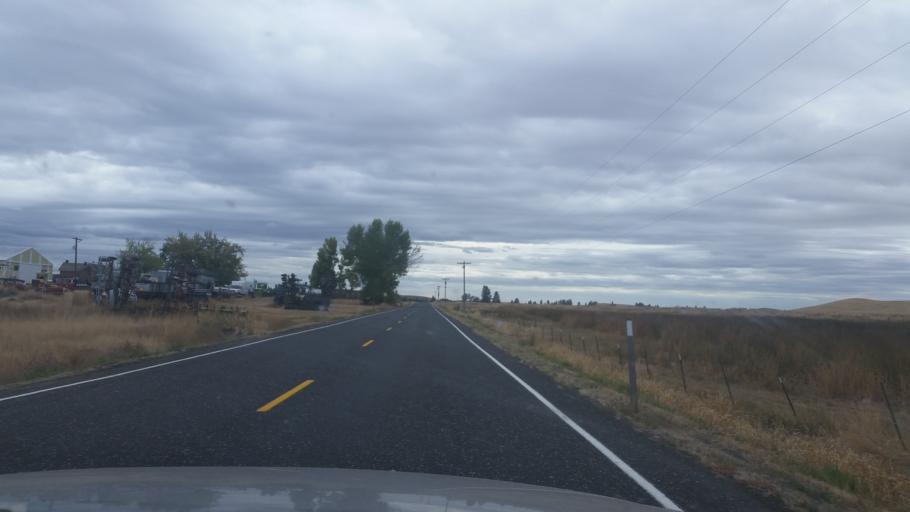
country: US
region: Washington
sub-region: Spokane County
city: Medical Lake
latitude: 47.5381
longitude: -117.8437
